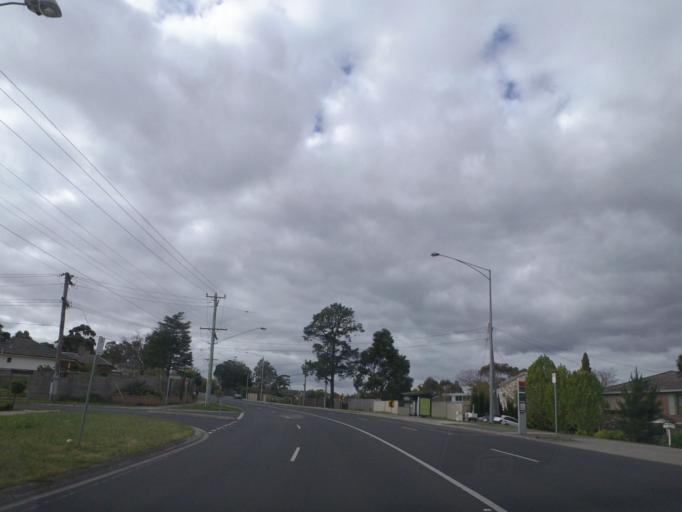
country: AU
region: Victoria
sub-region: Manningham
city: Templestowe Lower
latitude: -37.7795
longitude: 145.1129
